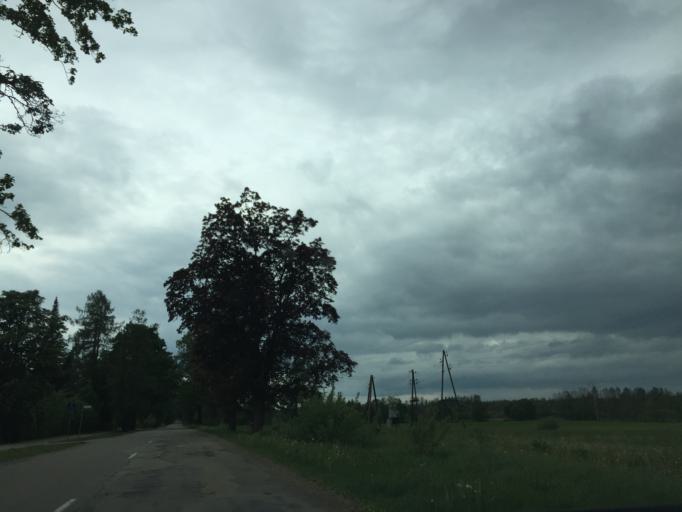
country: LV
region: Preilu Rajons
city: Preili
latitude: 56.0711
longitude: 26.7461
